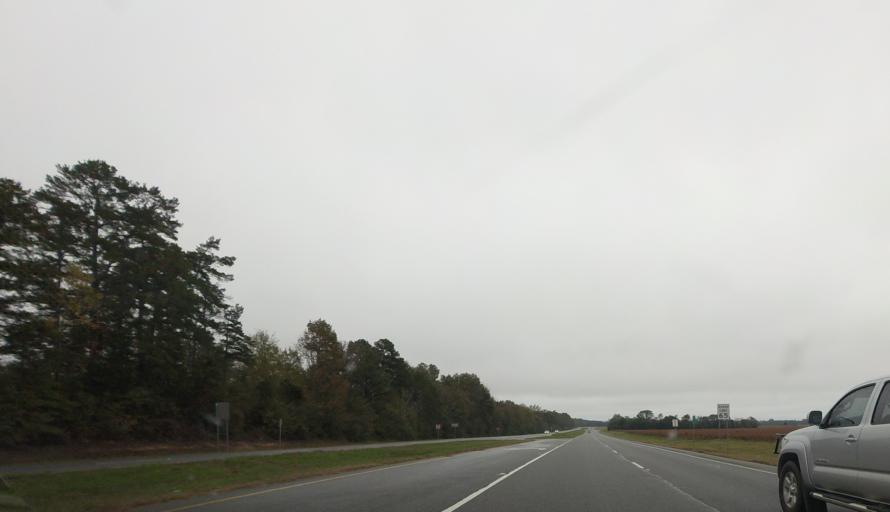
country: US
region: Georgia
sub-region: Taylor County
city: Reynolds
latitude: 32.5588
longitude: -84.0773
